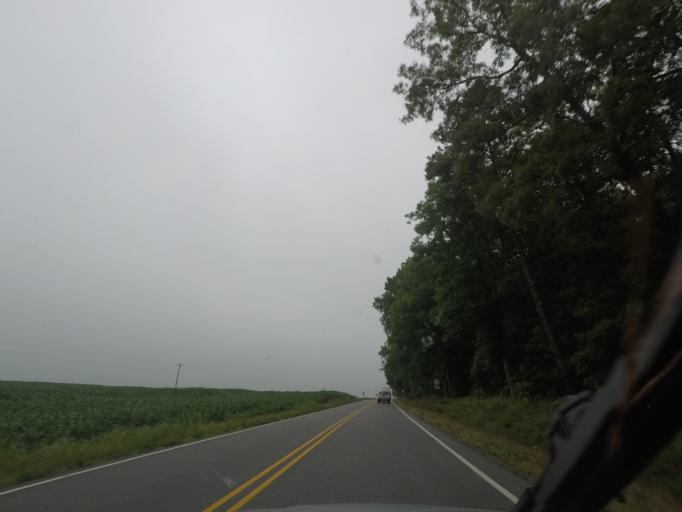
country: US
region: Virginia
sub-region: Prince Edward County
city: Farmville
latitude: 37.3583
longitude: -78.4828
